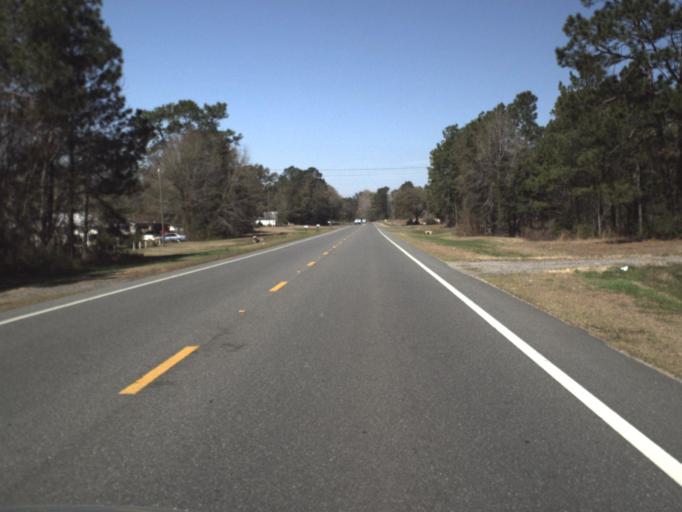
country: US
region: Florida
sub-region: Jackson County
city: Marianna
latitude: 30.7273
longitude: -85.0861
